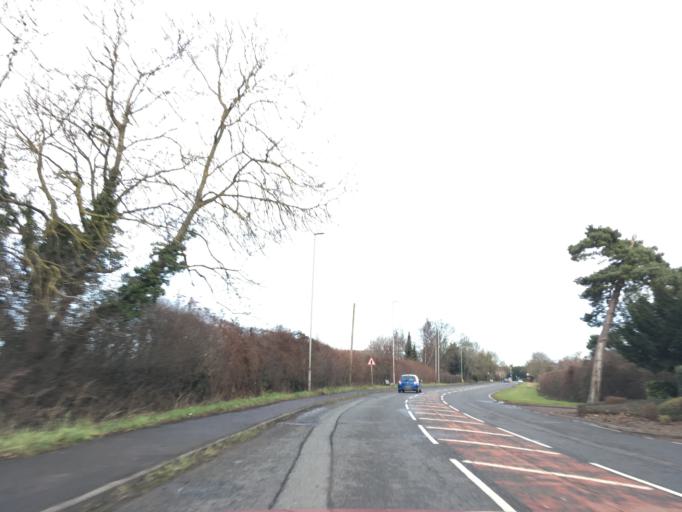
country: GB
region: England
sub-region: Nottinghamshire
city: Ruddington
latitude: 52.8631
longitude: -1.1338
